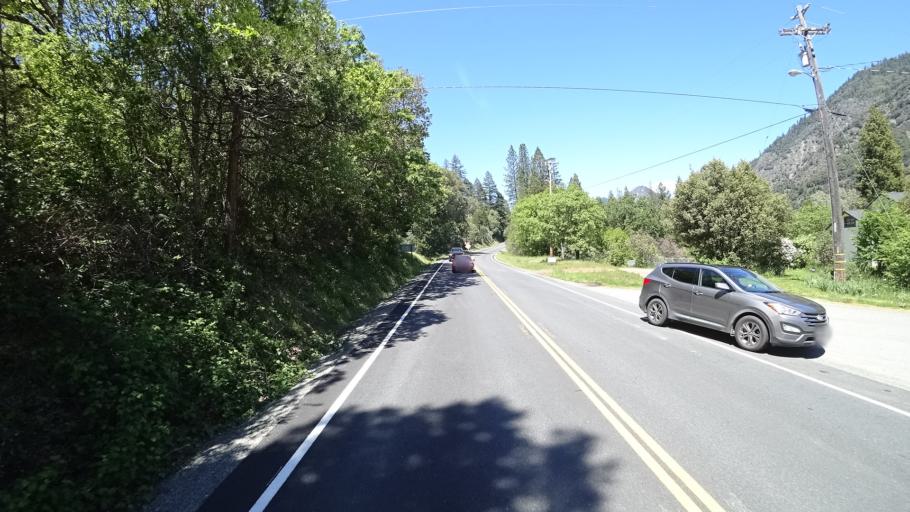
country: US
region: California
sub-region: Humboldt County
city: Willow Creek
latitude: 40.8226
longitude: -123.4837
